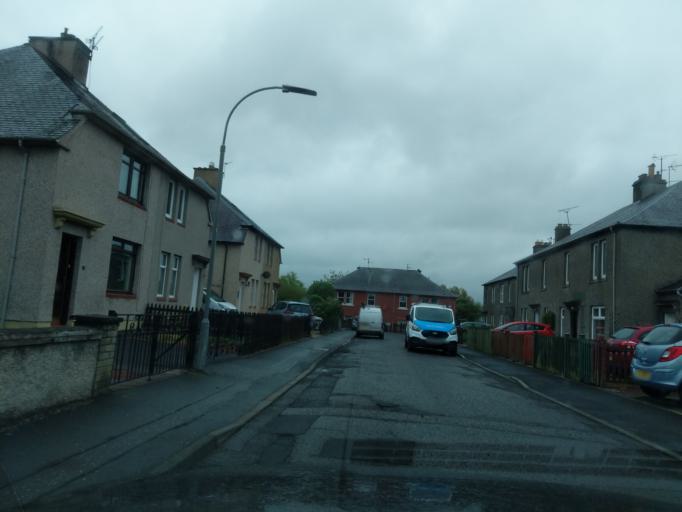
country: GB
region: Scotland
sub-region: The Scottish Borders
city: Kelso
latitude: 55.6012
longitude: -2.4328
